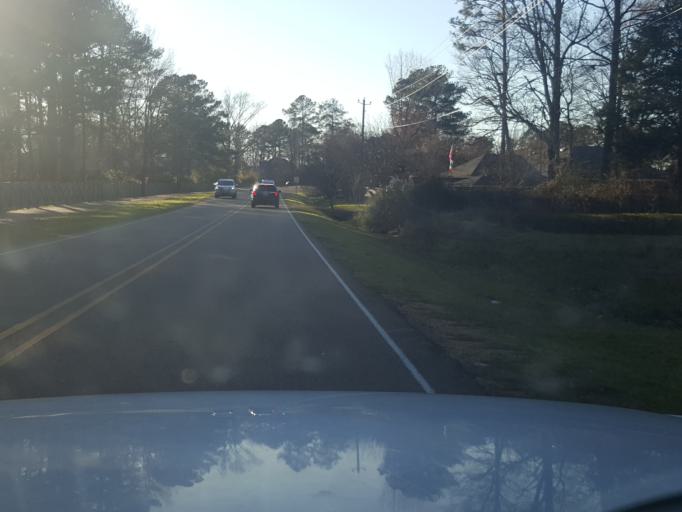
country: US
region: Mississippi
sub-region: Madison County
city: Madison
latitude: 32.4136
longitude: -90.0174
